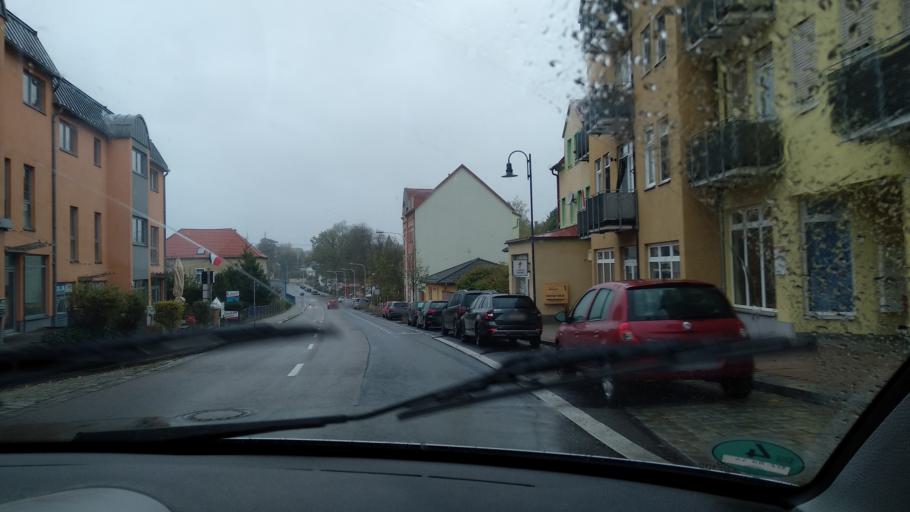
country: DE
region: Saxony
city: Radeberg
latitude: 51.1147
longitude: 13.9105
